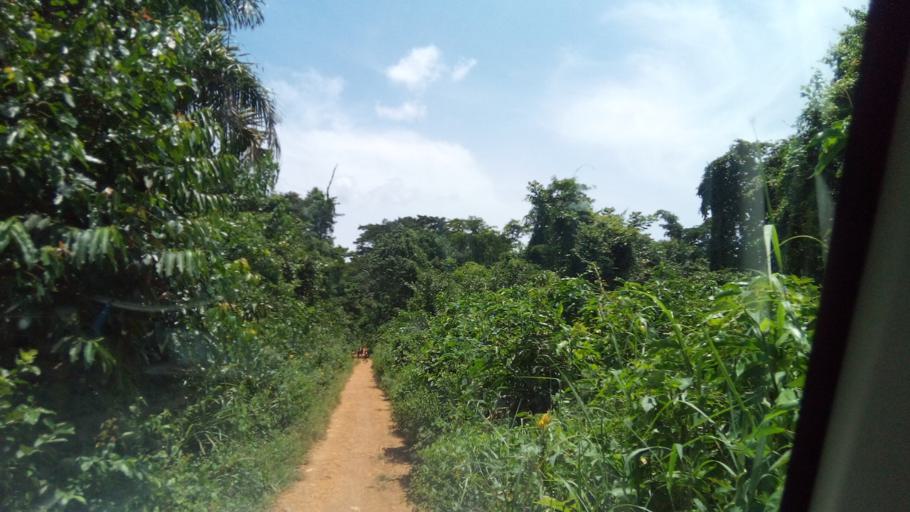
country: AO
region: Zaire
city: Mbanza Congo
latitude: -5.8065
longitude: 14.2449
